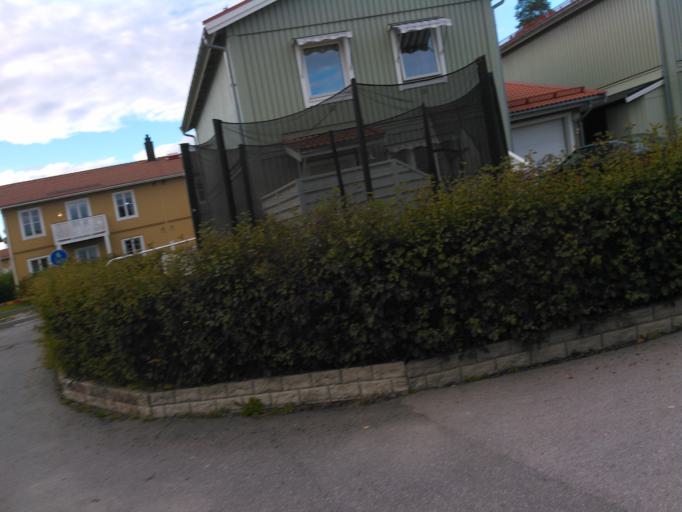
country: SE
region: Vaesterbotten
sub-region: Umea Kommun
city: Ersmark
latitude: 63.8059
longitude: 20.3382
